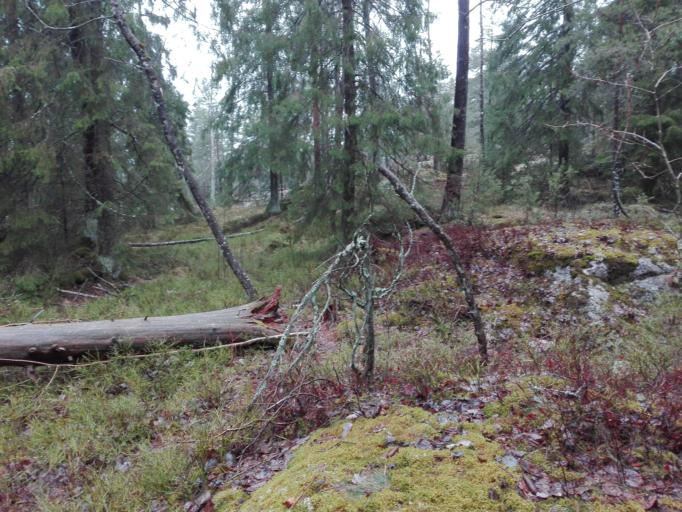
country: SE
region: Stockholm
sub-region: Nacka Kommun
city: Fisksatra
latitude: 59.2771
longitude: 18.2589
